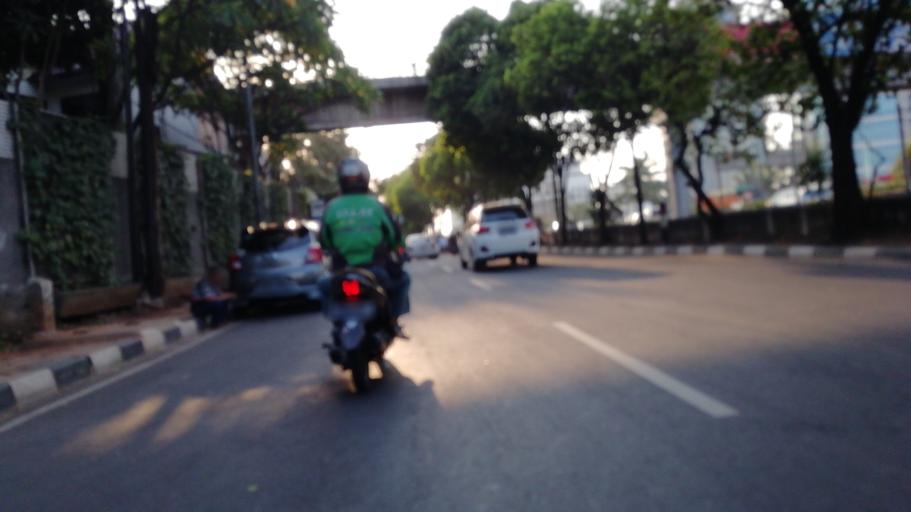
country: ID
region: Jakarta Raya
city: Jakarta
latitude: -6.2924
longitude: 106.8128
